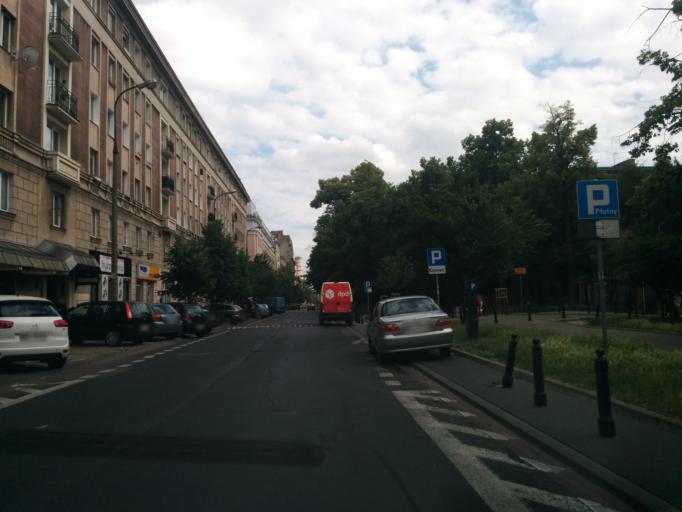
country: PL
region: Masovian Voivodeship
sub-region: Warszawa
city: Srodmiescie
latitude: 52.2163
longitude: 21.0175
